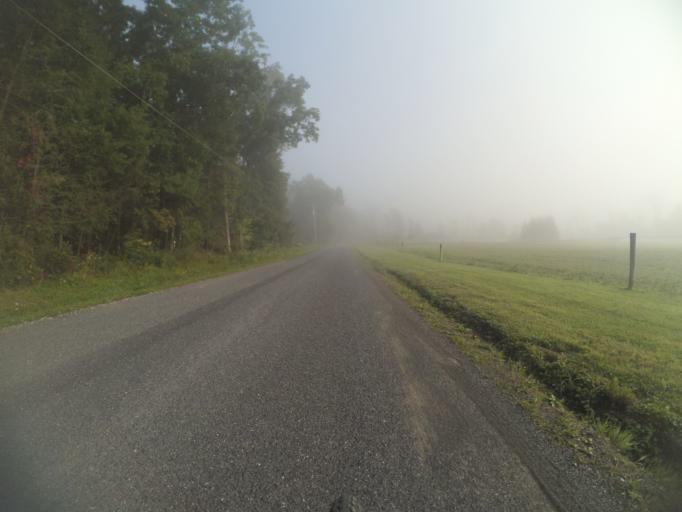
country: US
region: Pennsylvania
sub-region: Centre County
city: Zion
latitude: 40.8908
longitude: -77.5040
